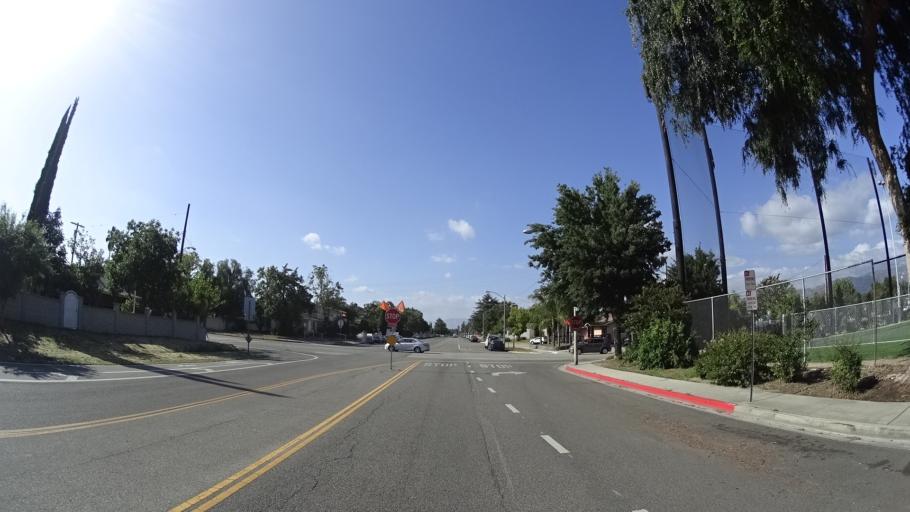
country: US
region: California
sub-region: Los Angeles County
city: North Hollywood
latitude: 34.1791
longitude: -118.3588
